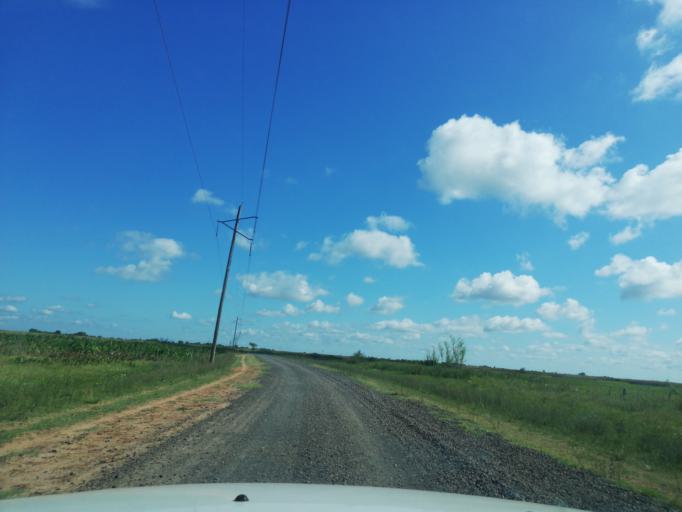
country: AR
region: Corrientes
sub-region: Departamento de San Miguel
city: San Miguel
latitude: -27.9813
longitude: -57.5808
